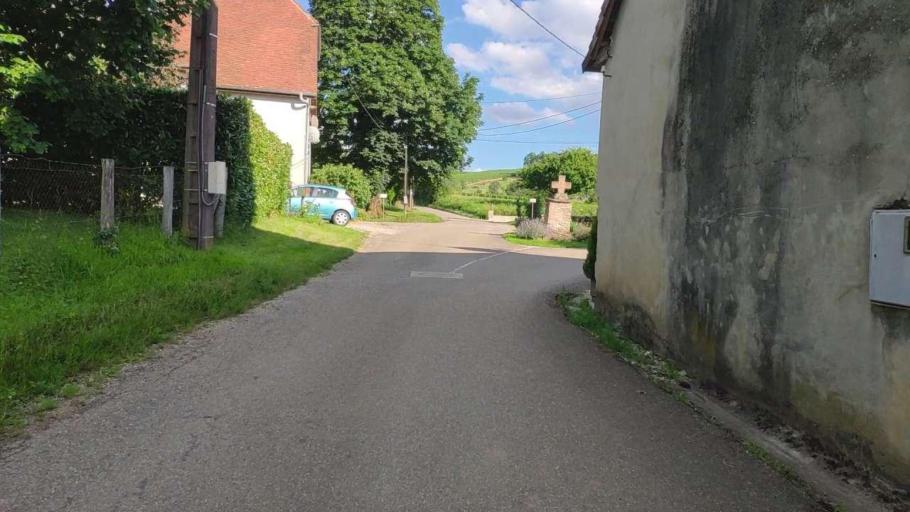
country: FR
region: Franche-Comte
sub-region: Departement du Jura
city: Bletterans
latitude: 46.7510
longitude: 5.5219
